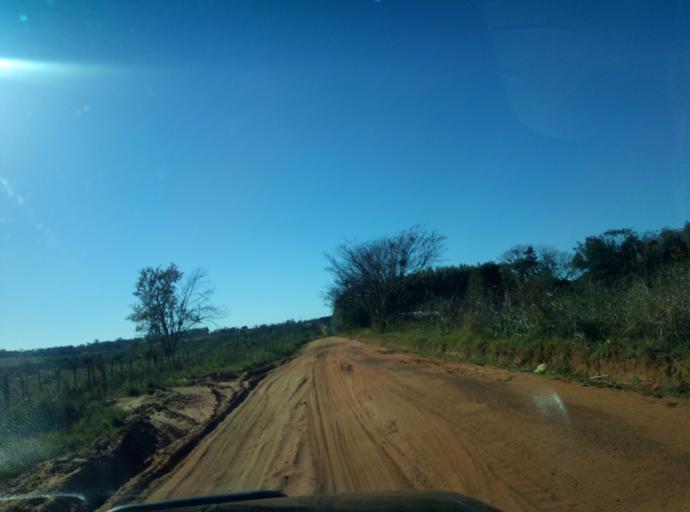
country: PY
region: Caaguazu
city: Doctor Cecilio Baez
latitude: -25.1628
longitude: -56.2640
